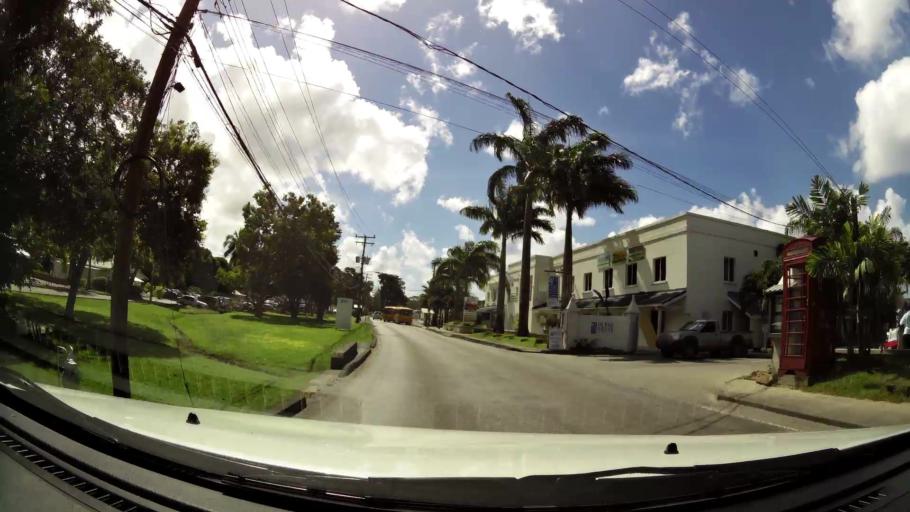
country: BB
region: Saint James
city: Holetown
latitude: 13.1835
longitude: -59.6386
